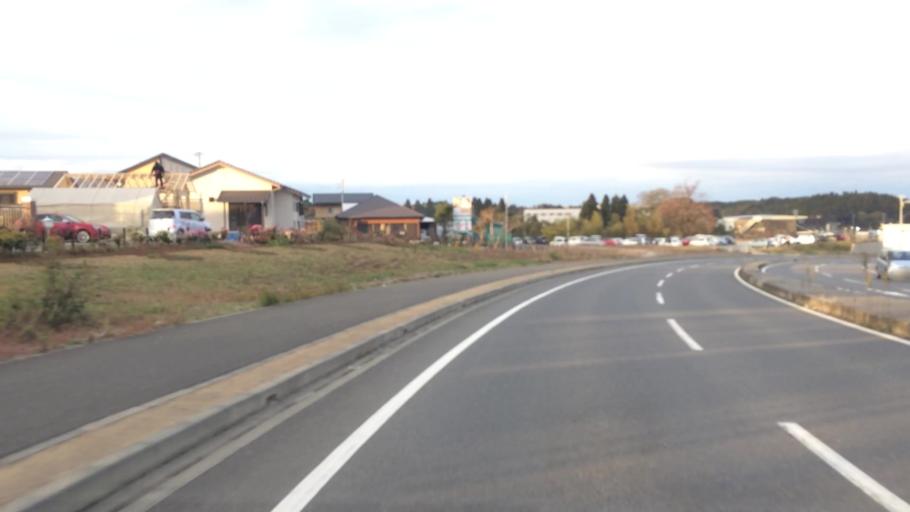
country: JP
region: Chiba
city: Shisui
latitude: 35.7147
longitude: 140.2920
